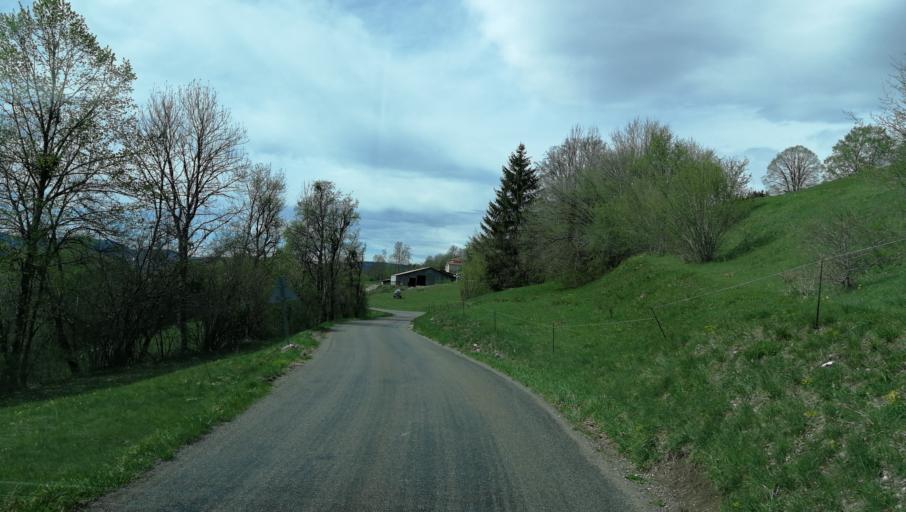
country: FR
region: Rhone-Alpes
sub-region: Departement de l'Ain
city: Arbent
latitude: 46.2458
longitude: 5.7723
